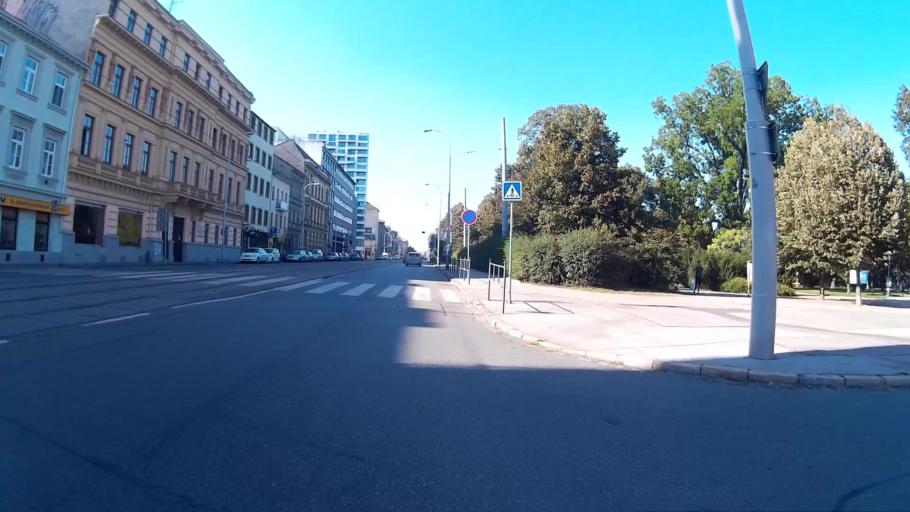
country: CZ
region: South Moravian
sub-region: Mesto Brno
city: Brno
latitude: 49.2042
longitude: 16.6066
